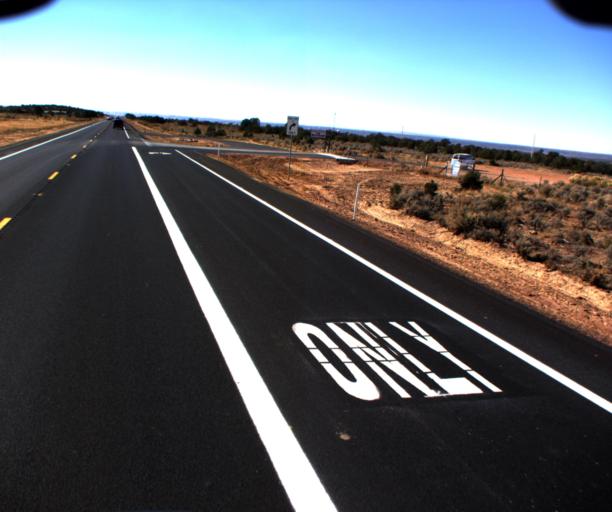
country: US
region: Arizona
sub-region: Apache County
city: Ganado
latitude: 35.7177
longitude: -109.4023
